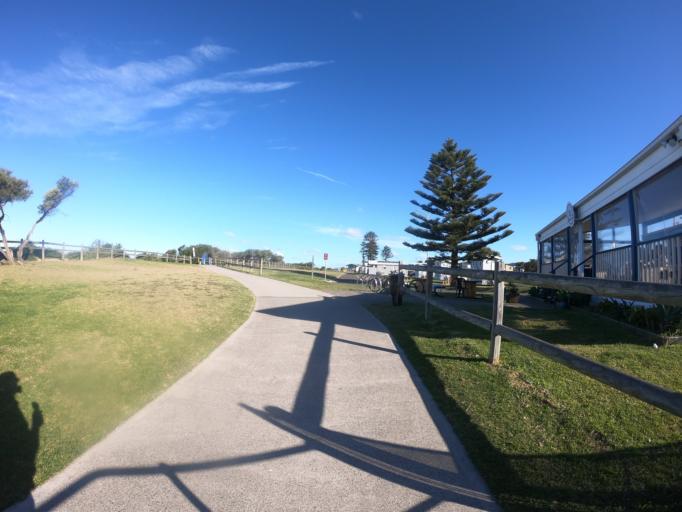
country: AU
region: New South Wales
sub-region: Wollongong
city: Bulli
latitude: -34.3409
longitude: 150.9238
